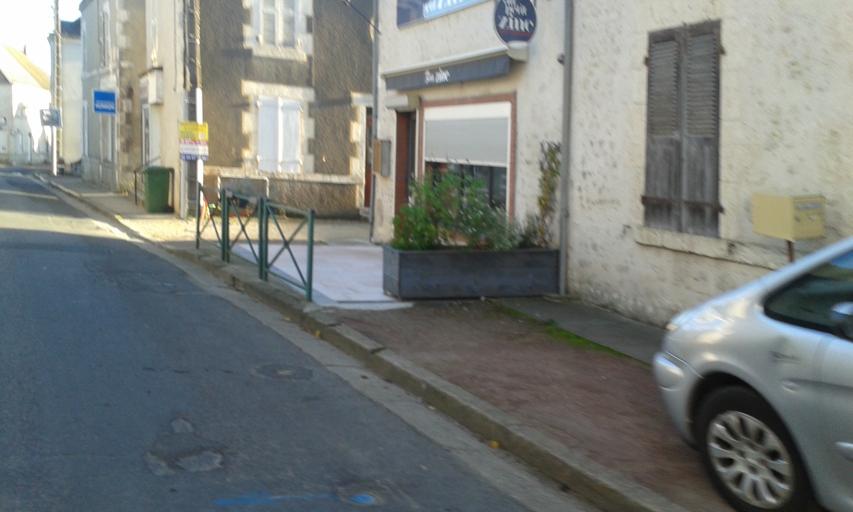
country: FR
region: Centre
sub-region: Departement du Loir-et-Cher
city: Mer
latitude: 47.7970
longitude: 1.5236
